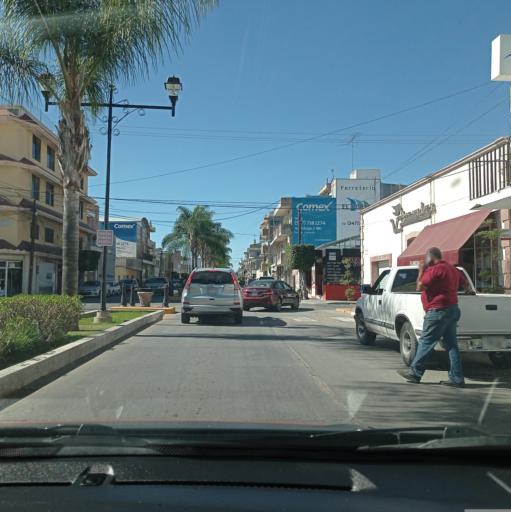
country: MX
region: Jalisco
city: San Julian
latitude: 21.0100
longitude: -102.1766
